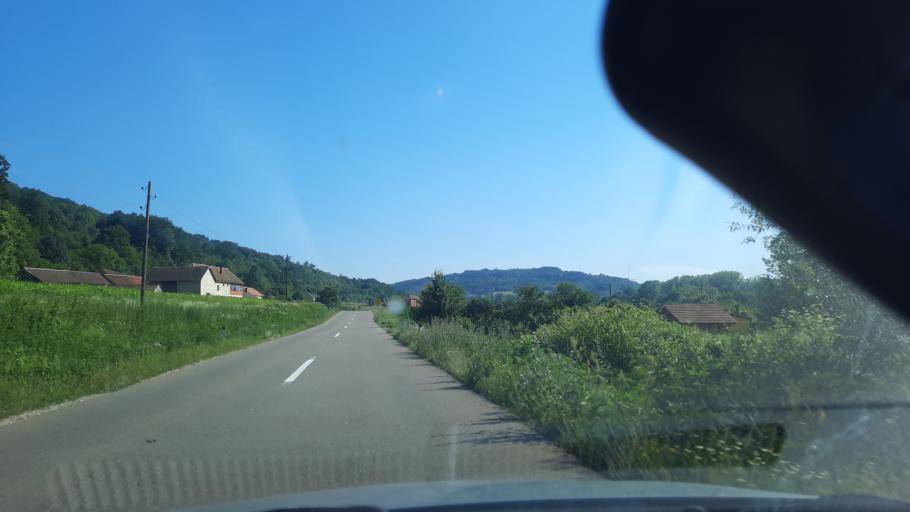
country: RS
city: Turija
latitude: 44.5046
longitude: 21.6323
